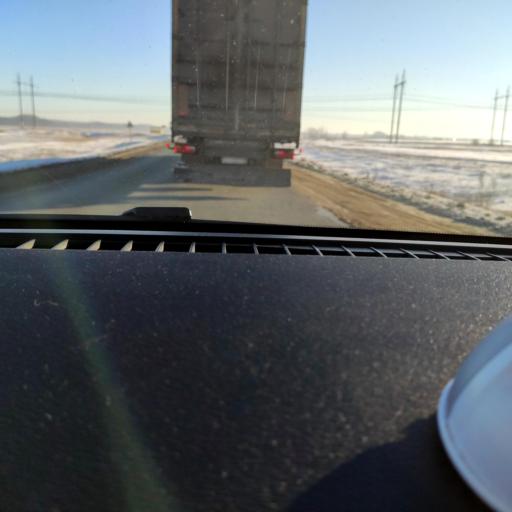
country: RU
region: Samara
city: Spiridonovka
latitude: 53.1428
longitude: 50.5918
